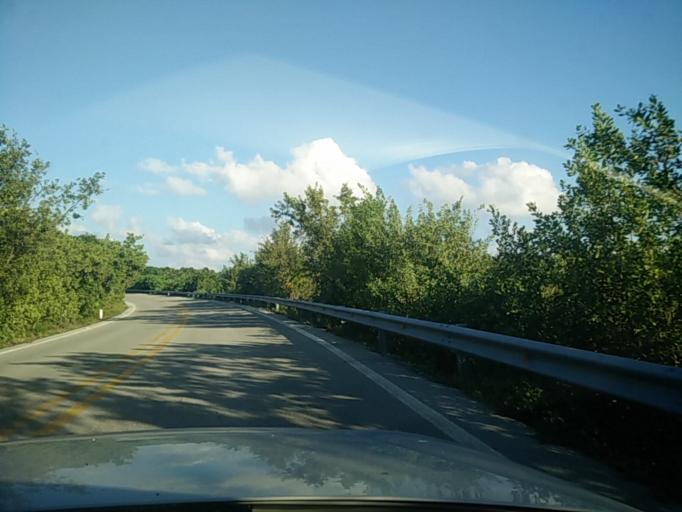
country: MX
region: Quintana Roo
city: San Miguel de Cozumel
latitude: 20.3468
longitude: -86.9007
